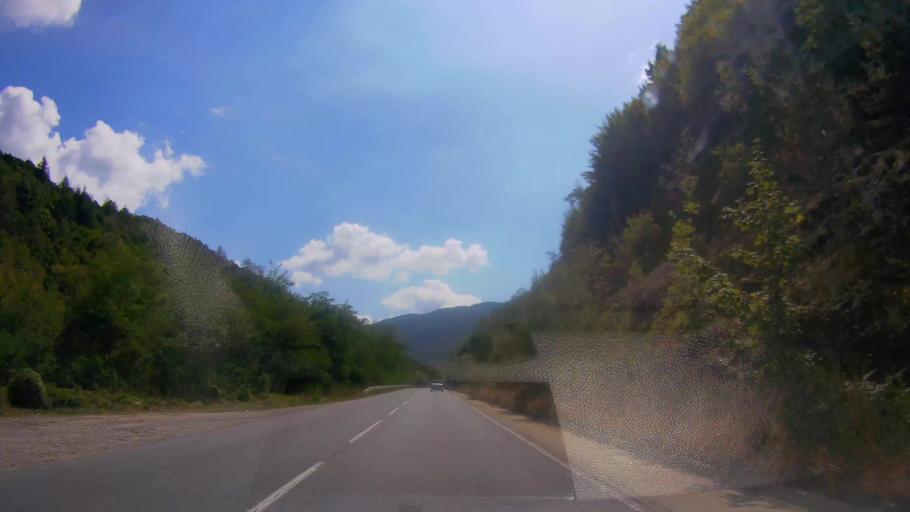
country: BG
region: Stara Zagora
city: Gurkovo
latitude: 42.7240
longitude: 25.7132
